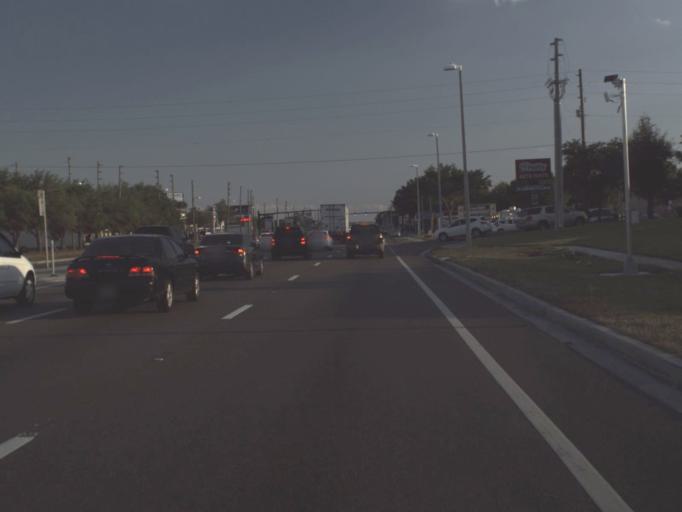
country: US
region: Florida
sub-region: Orange County
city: Southchase
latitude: 28.4002
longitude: -81.4047
